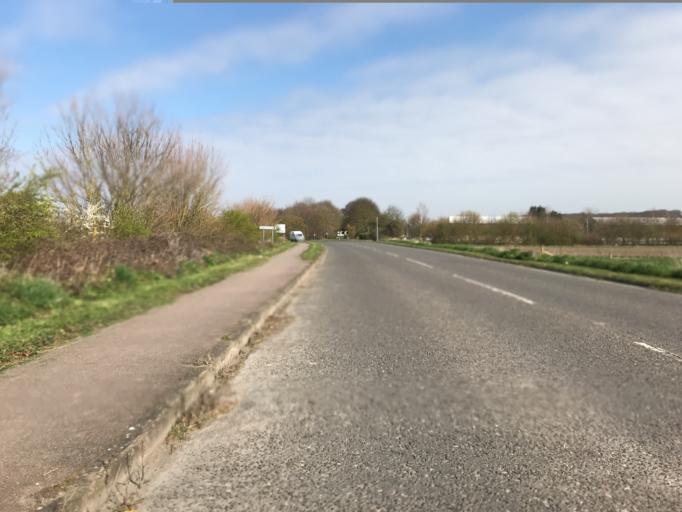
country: GB
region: England
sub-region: Cambridgeshire
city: Sawston
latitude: 52.1631
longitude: 0.1591
